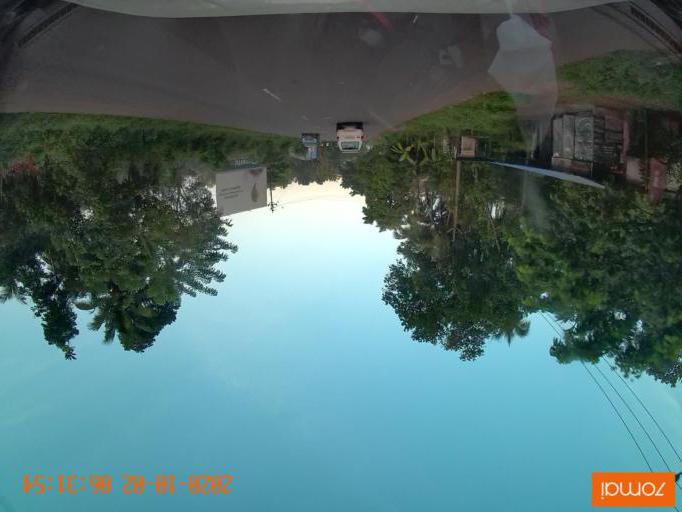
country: IN
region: Kerala
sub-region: Malappuram
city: Ponnani
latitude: 10.7473
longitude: 76.0261
